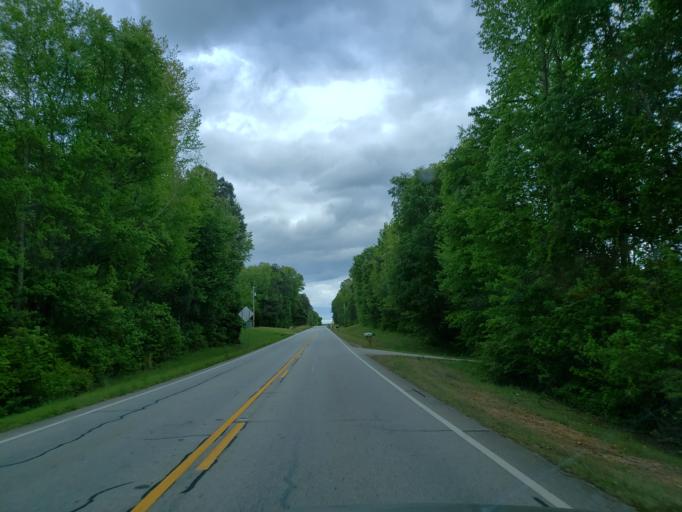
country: US
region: Georgia
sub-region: Carroll County
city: Temple
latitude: 33.8203
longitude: -85.0872
